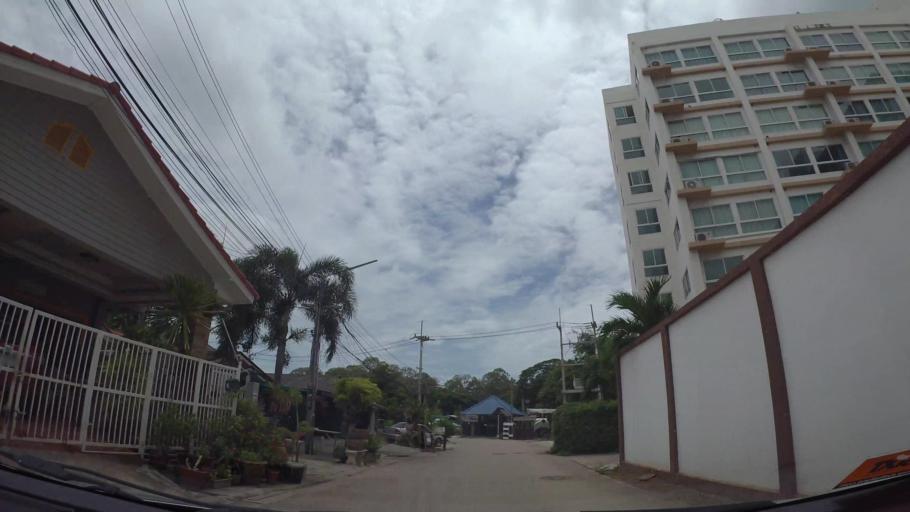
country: TH
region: Chon Buri
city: Sattahip
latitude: 12.7649
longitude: 100.8967
